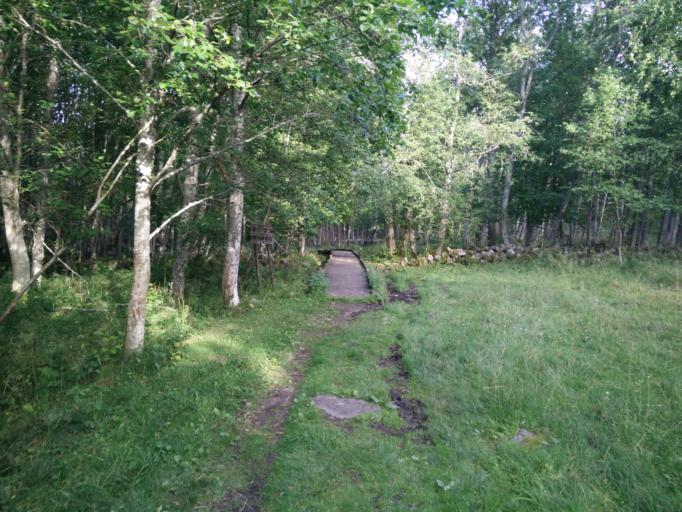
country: SE
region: Vaesternorrland
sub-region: Timra Kommun
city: Soraker
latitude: 62.4508
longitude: 17.4844
